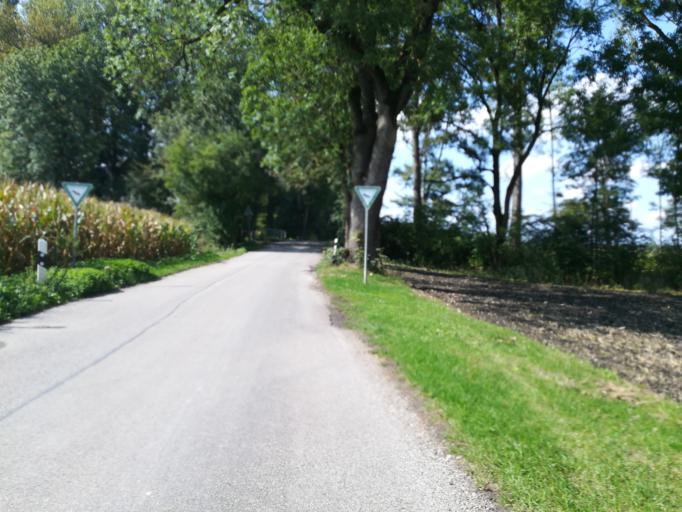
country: DE
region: Bavaria
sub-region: Upper Bavaria
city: Karlsfeld
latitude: 48.2270
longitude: 11.5114
